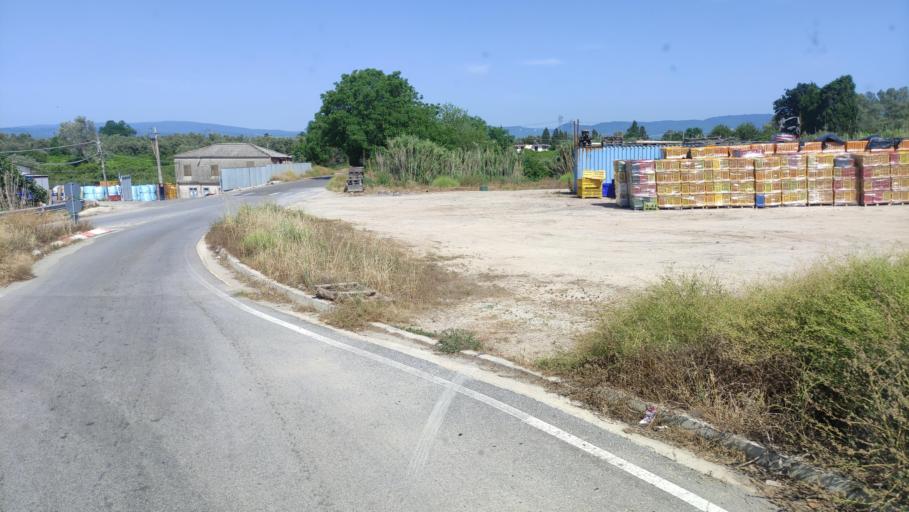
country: IT
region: Calabria
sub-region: Provincia di Reggio Calabria
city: Rosarno
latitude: 38.4540
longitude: 15.9825
